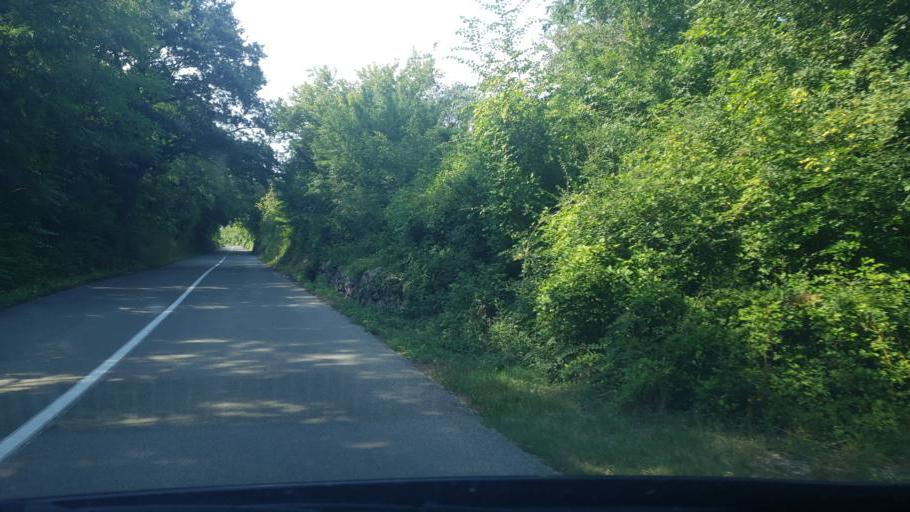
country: HR
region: Primorsko-Goranska
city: Punat
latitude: 45.0926
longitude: 14.6435
